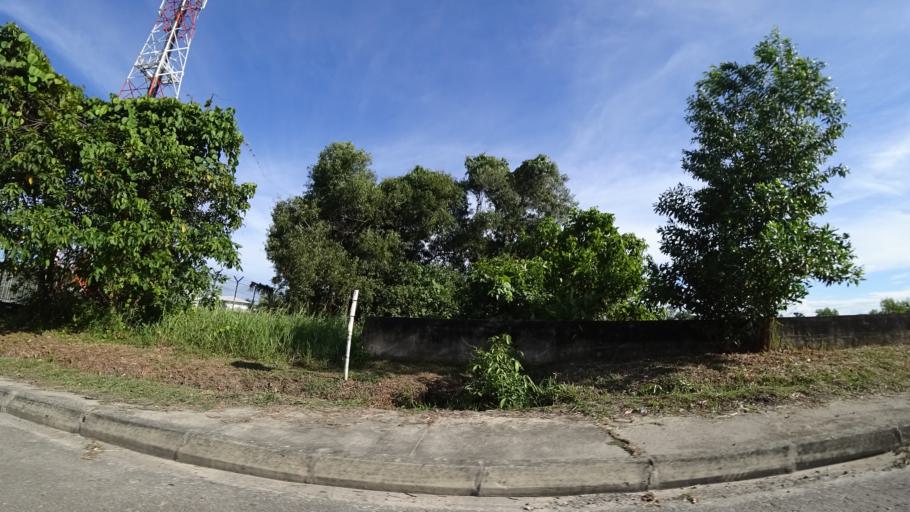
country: BN
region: Brunei and Muara
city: Bandar Seri Begawan
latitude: 4.9760
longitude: 114.9775
